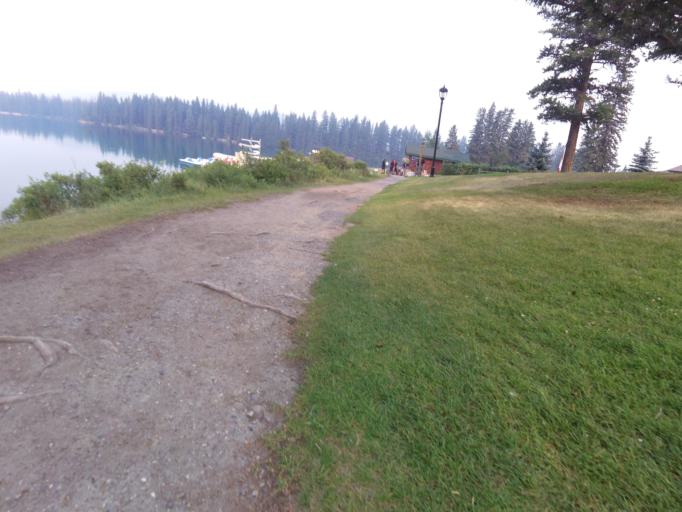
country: CA
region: Alberta
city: Jasper Park Lodge
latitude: 52.8848
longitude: -118.0567
